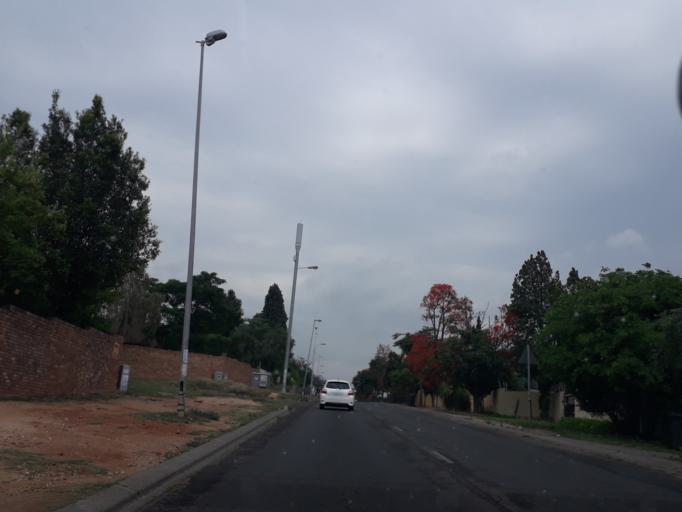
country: ZA
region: Gauteng
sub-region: West Rand District Municipality
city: Muldersdriseloop
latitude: -26.0701
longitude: 27.9448
